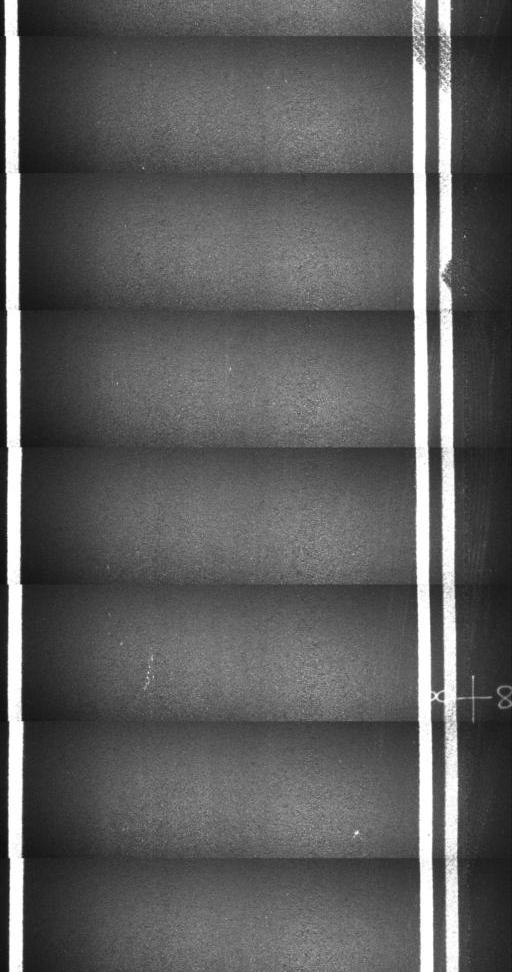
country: US
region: Vermont
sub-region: Orange County
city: Randolph
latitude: 43.8643
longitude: -72.6465
